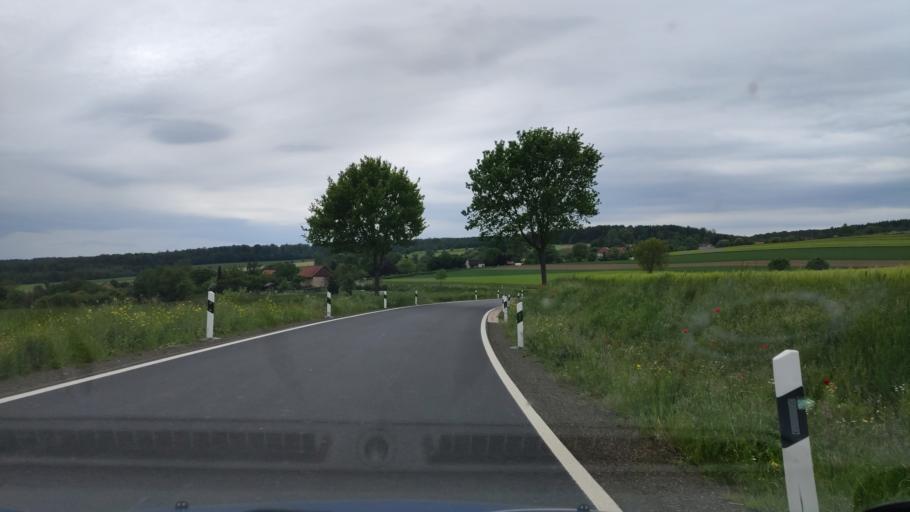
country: DE
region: Lower Saxony
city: Hardegsen
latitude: 51.7051
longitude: 9.7844
